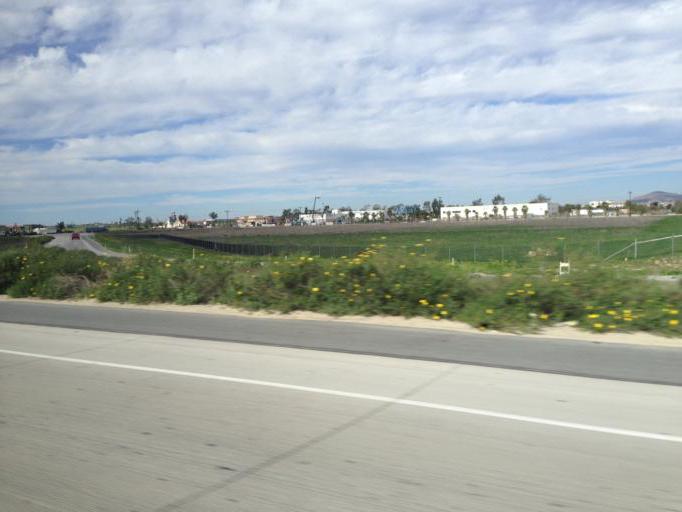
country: MX
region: Baja California
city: Tijuana
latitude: 32.5643
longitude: -116.9576
